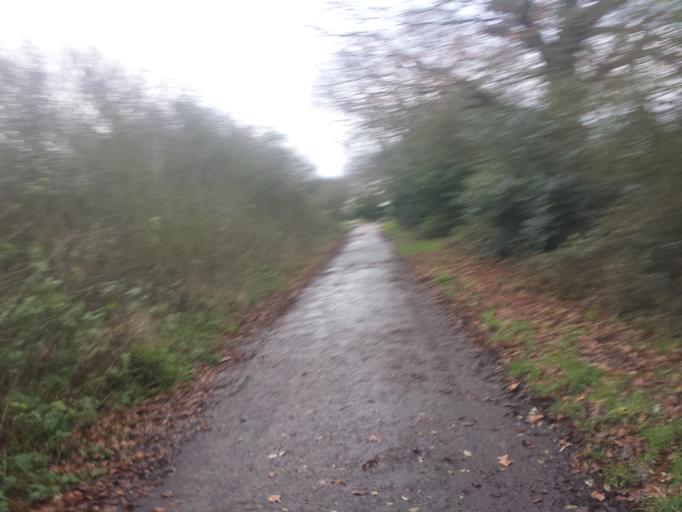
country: GB
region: England
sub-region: Essex
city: Great Bentley
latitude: 51.8843
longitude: 1.0362
